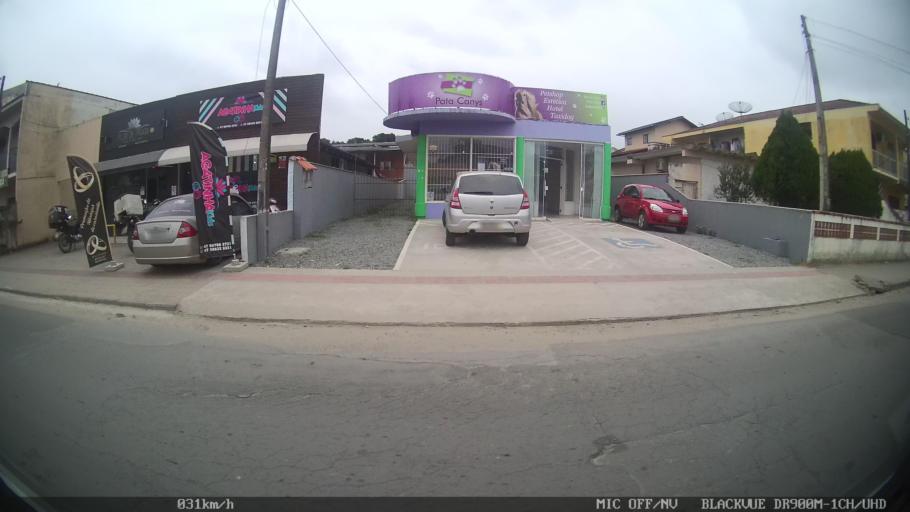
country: BR
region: Santa Catarina
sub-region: Joinville
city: Joinville
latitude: -26.3619
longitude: -48.8295
